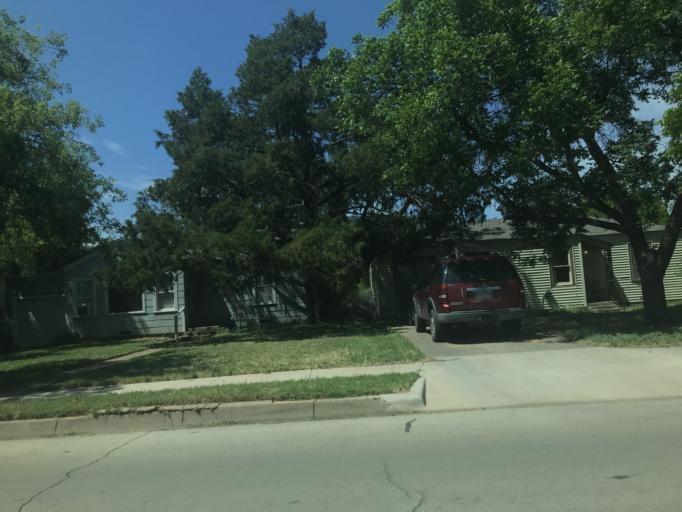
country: US
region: Texas
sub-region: Taylor County
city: Abilene
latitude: 32.4375
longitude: -99.7647
